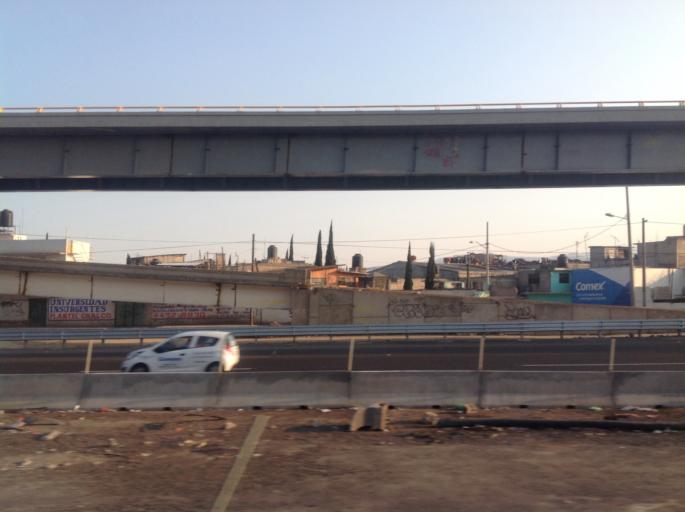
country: MX
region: Mexico
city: San Miguel Xico Viejo
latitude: 19.2906
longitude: -98.9172
